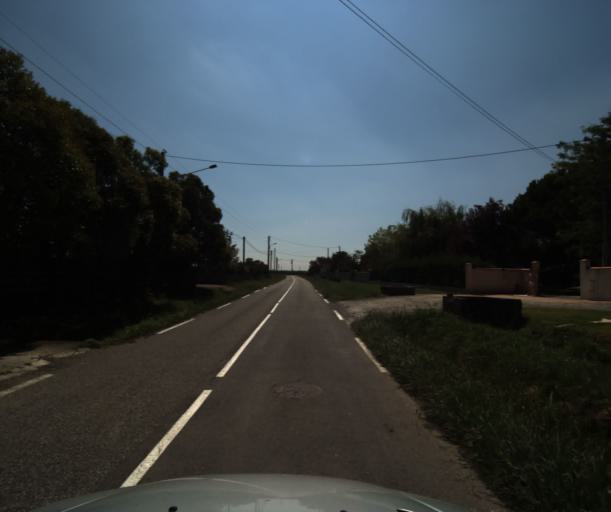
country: FR
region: Midi-Pyrenees
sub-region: Departement de la Haute-Garonne
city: Labastidette
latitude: 43.4392
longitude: 1.2570
